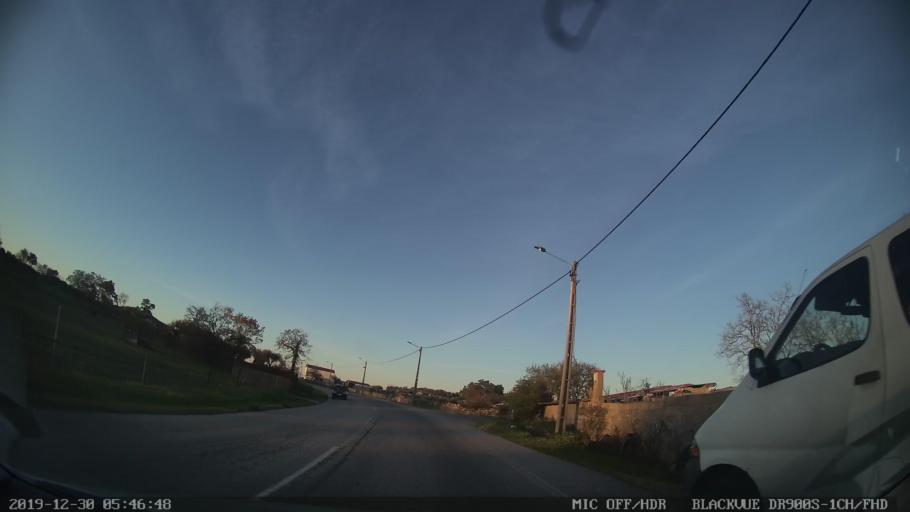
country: PT
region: Castelo Branco
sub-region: Idanha-A-Nova
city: Idanha-a-Nova
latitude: 39.9452
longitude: -7.2366
